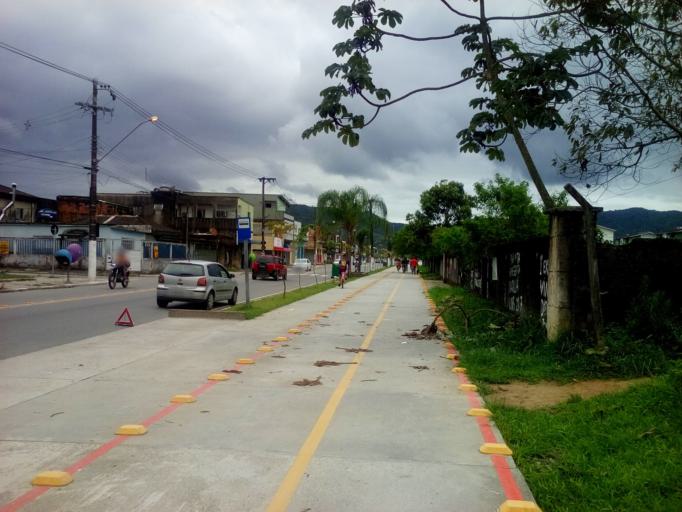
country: BR
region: Sao Paulo
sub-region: Guaruja
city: Guaruja
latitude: -23.9653
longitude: -46.2563
